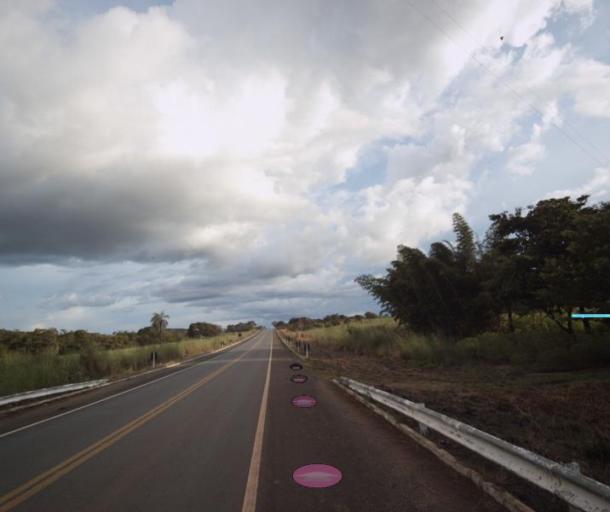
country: BR
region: Goias
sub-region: Barro Alto
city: Barro Alto
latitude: -14.8484
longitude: -48.6389
